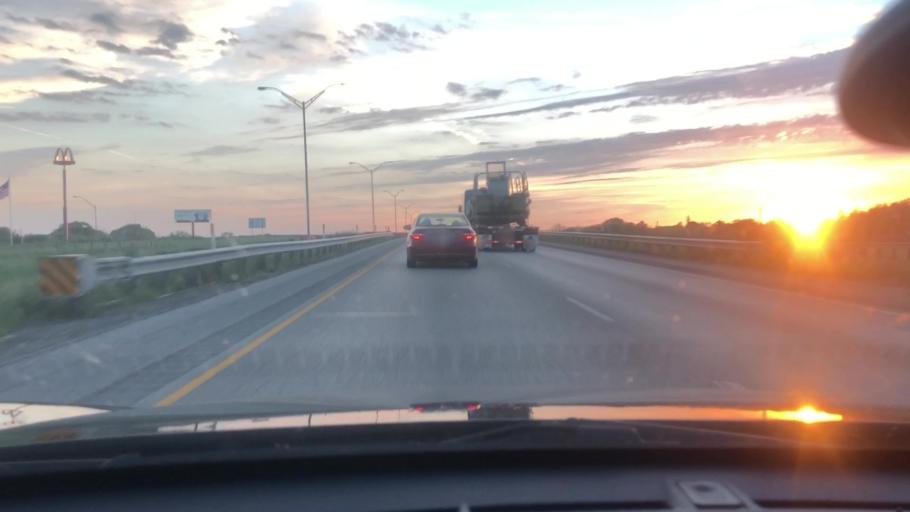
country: US
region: Texas
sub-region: Jackson County
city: Edna
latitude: 28.9872
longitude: -96.6495
